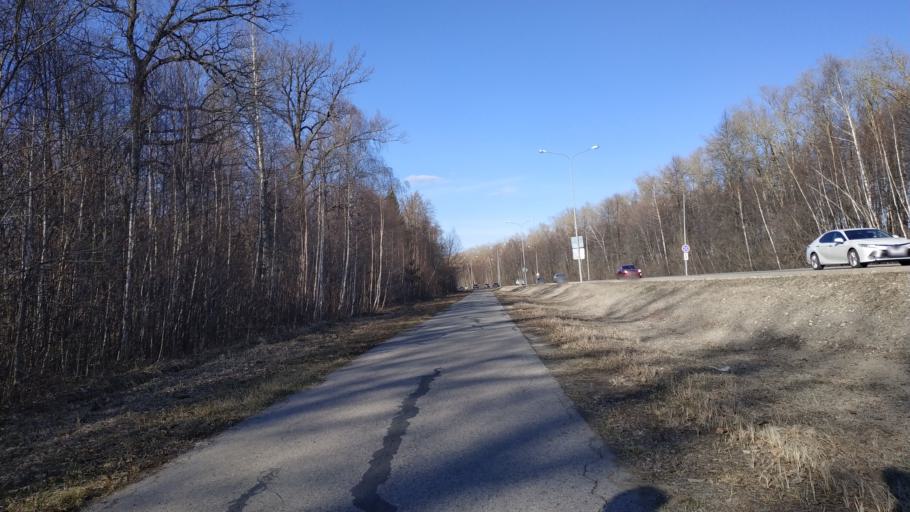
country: RU
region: Chuvashia
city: Ishley
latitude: 56.1275
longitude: 47.0676
